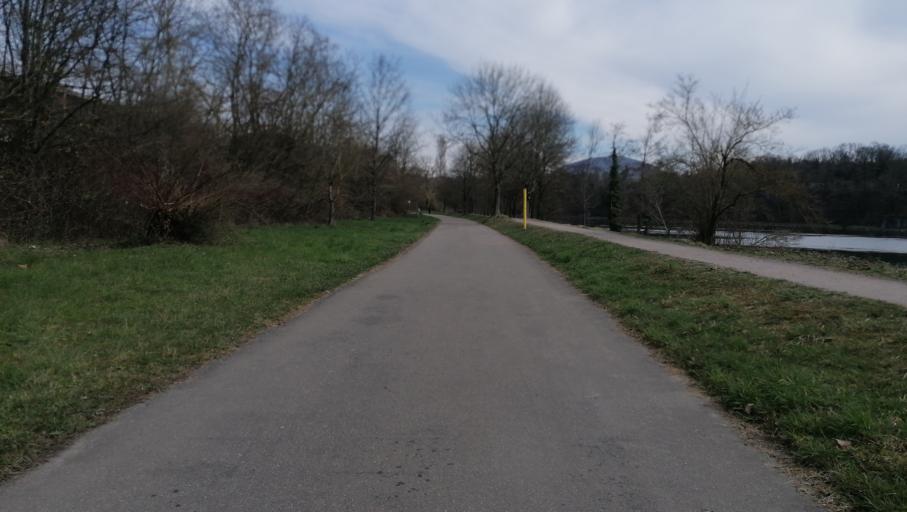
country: DE
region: Baden-Wuerttemberg
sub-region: Freiburg Region
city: Murg
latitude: 47.5525
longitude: 8.0149
